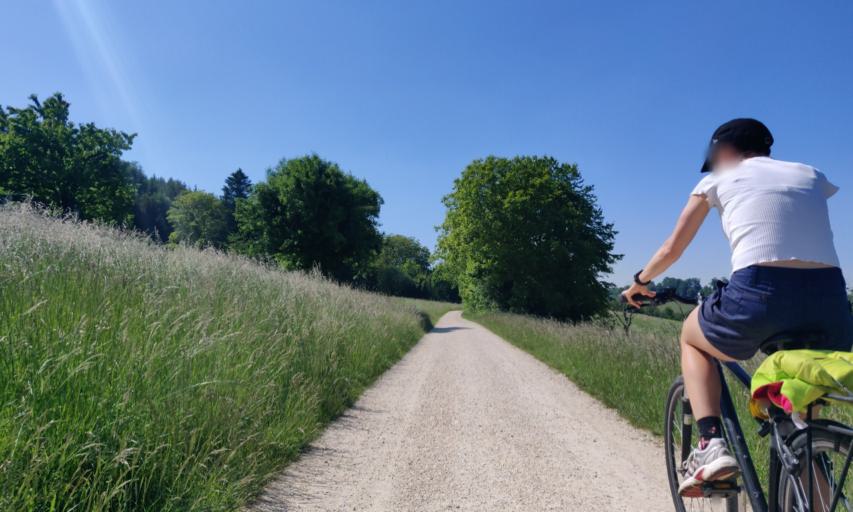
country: CH
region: Basel-Landschaft
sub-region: Bezirk Arlesheim
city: Pfeffingen
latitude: 47.4692
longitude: 7.5845
